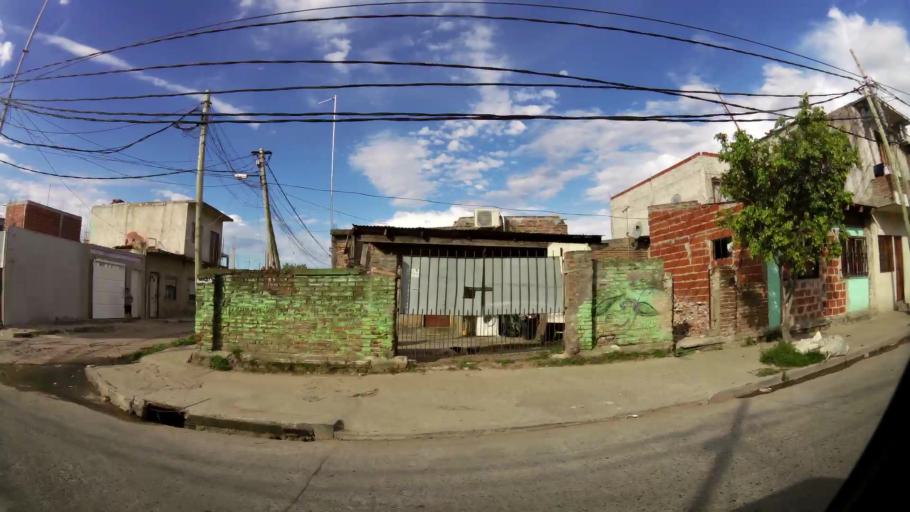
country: AR
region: Buenos Aires
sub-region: Partido de Lanus
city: Lanus
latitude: -34.7032
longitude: -58.3609
